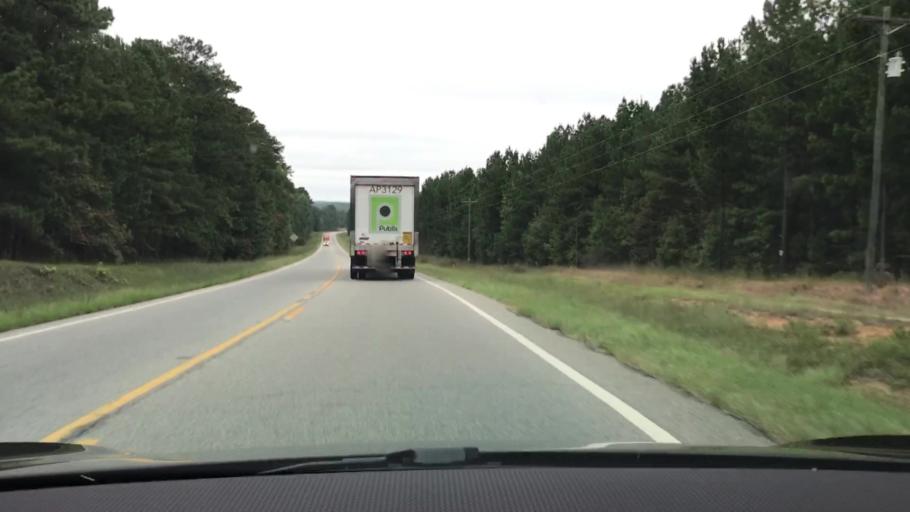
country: US
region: Georgia
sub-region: Greene County
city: Greensboro
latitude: 33.6643
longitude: -83.2463
